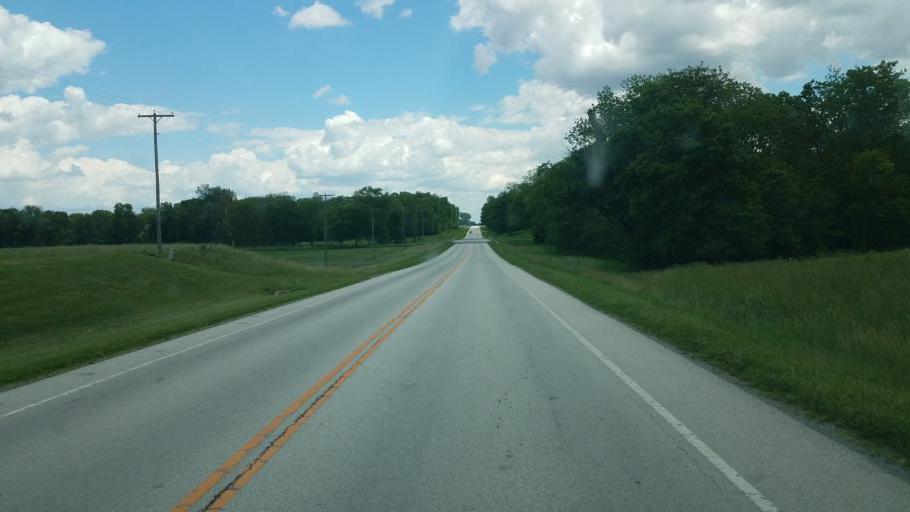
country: US
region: Ohio
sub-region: Wyandot County
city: Upper Sandusky
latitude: 40.8406
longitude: -83.1499
